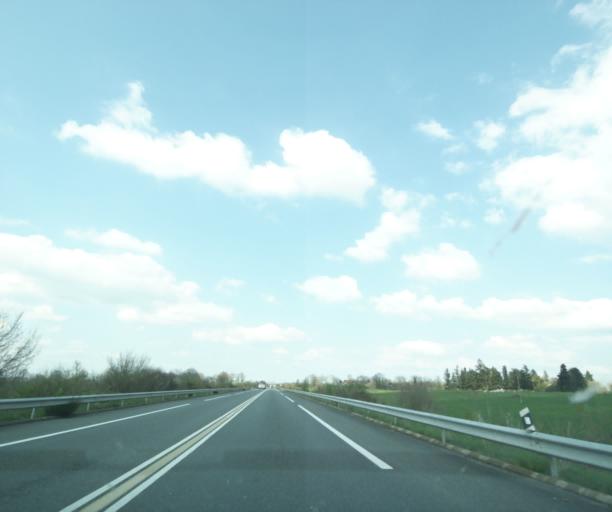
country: FR
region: Auvergne
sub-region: Departement de l'Allier
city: Montmarault
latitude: 46.3851
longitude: 3.0318
